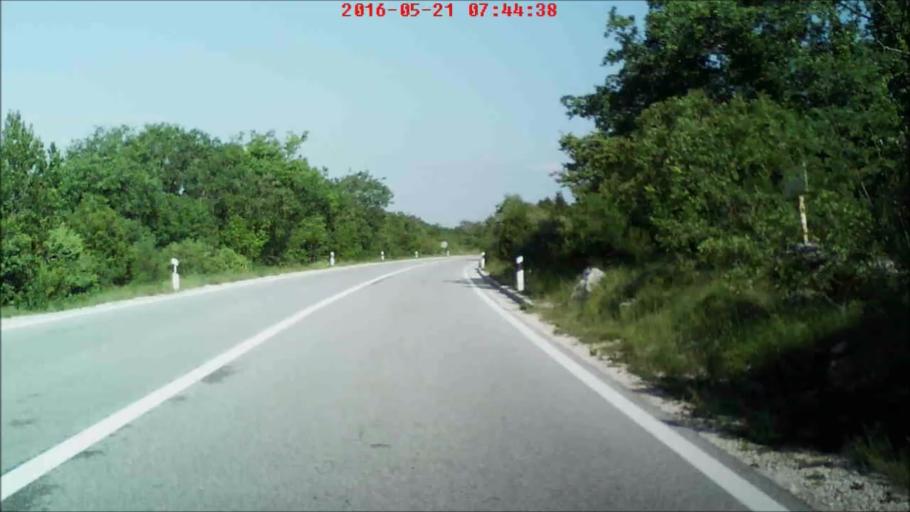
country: HR
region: Dubrovacko-Neretvanska
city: Podgora
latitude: 42.8172
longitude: 17.7761
